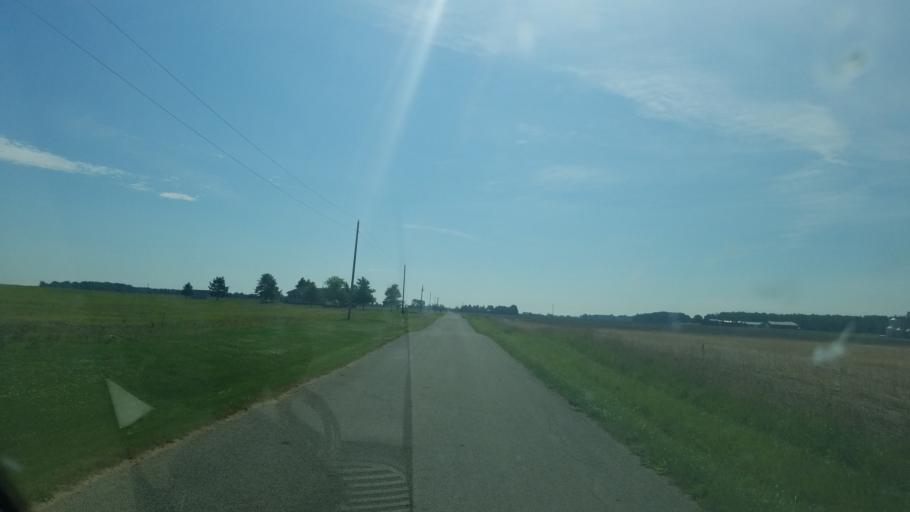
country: US
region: Ohio
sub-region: Wyandot County
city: Carey
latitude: 41.0142
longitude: -83.3458
